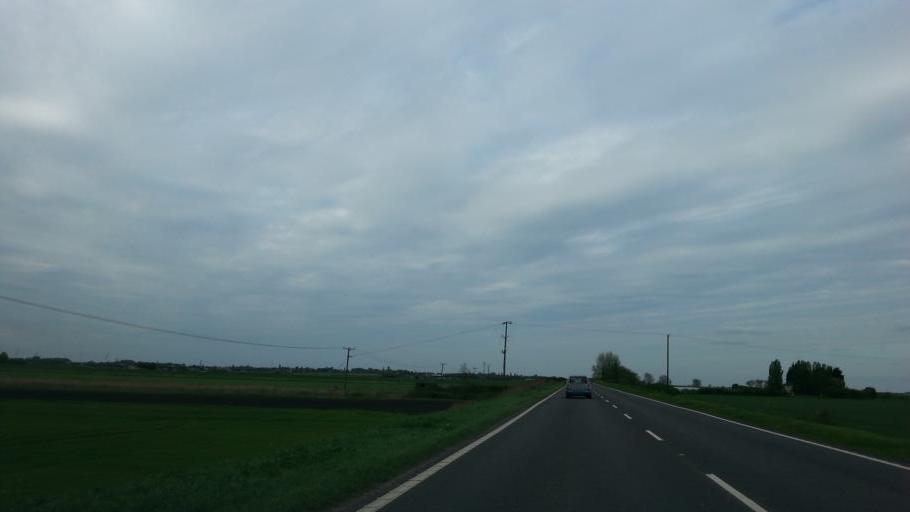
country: GB
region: England
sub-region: Cambridgeshire
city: Chatteris
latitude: 52.4702
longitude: 0.0478
